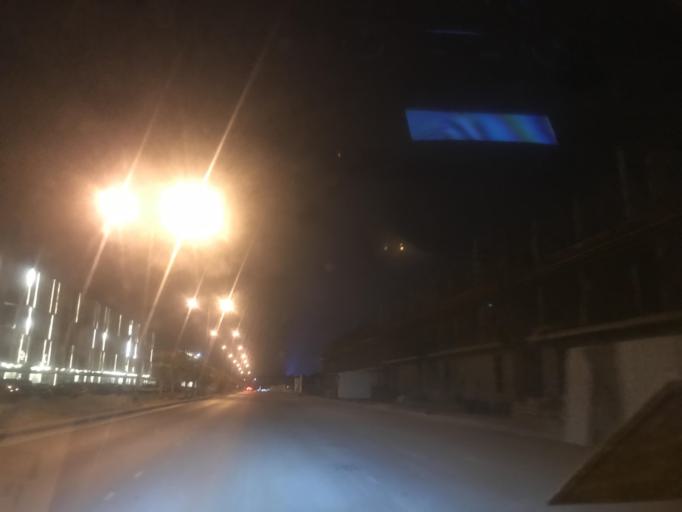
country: SA
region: Ar Riyad
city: Riyadh
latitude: 24.8020
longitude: 46.5926
